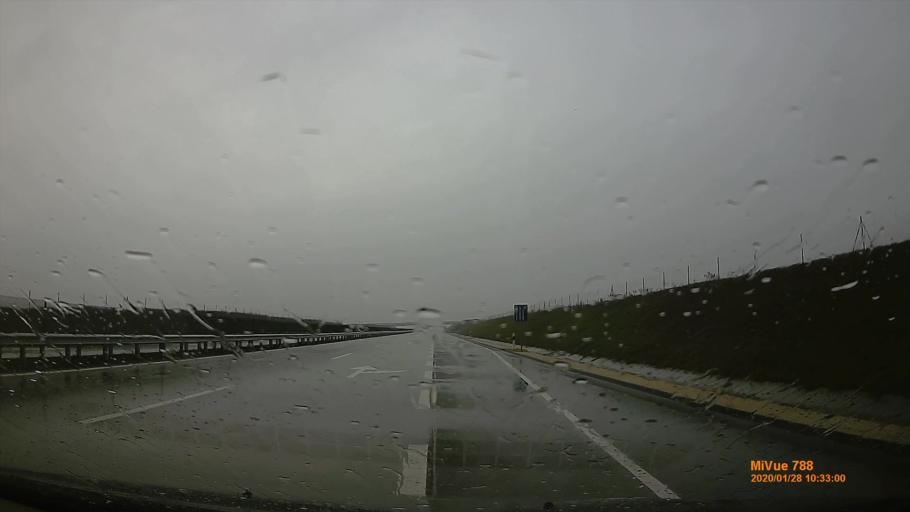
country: HU
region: Pest
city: Monor
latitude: 47.3552
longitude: 19.4884
